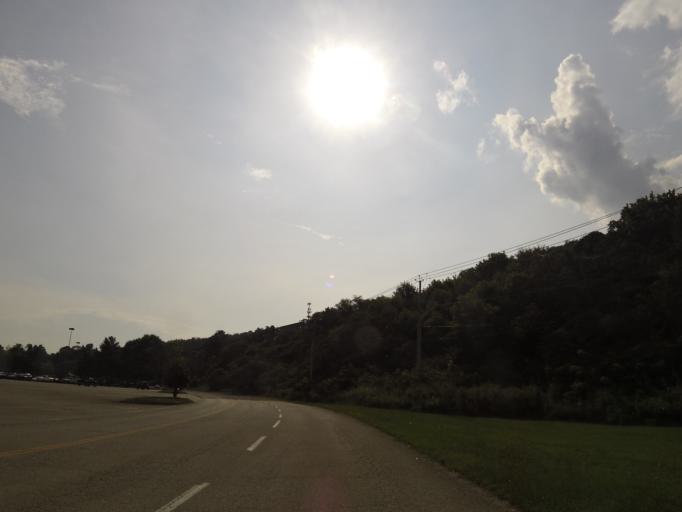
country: US
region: Tennessee
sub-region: Knox County
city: Knoxville
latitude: 36.0362
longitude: -83.8756
